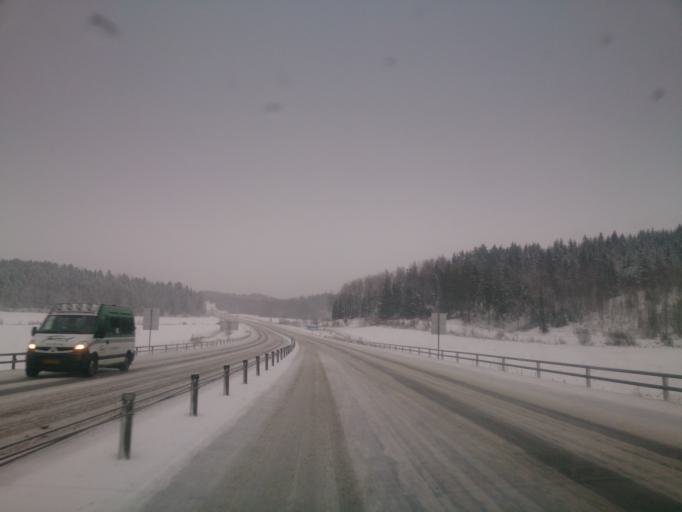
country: SE
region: OEstergoetland
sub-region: Norrkopings Kommun
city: Svartinge
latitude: 58.6718
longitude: 15.9636
